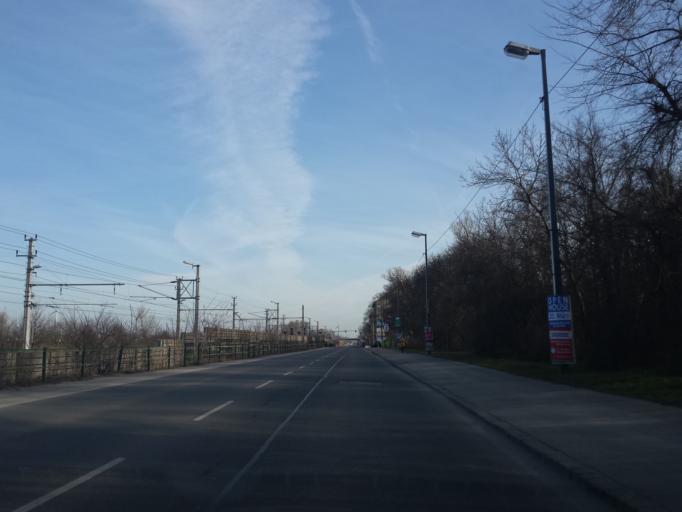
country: AT
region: Lower Austria
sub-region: Politischer Bezirk Wien-Umgebung
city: Schwechat
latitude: 48.1989
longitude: 16.4425
